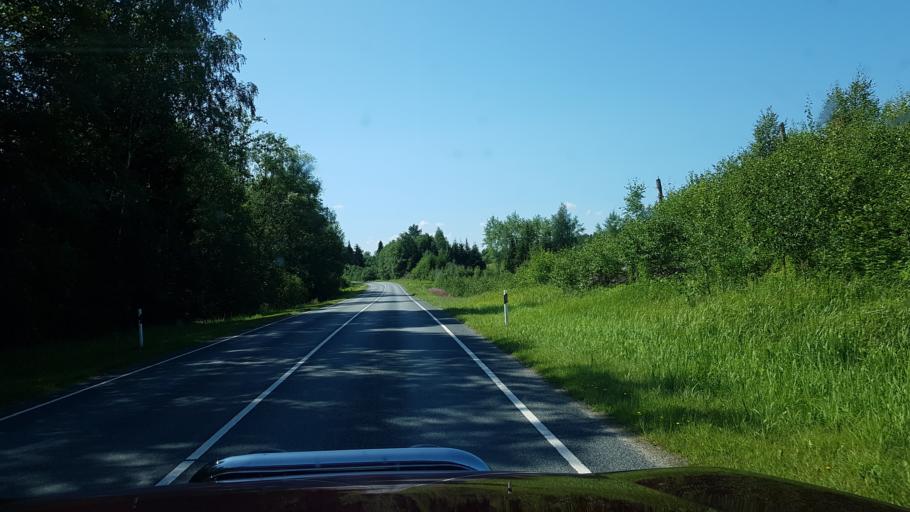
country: EE
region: Vorumaa
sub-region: Antsla vald
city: Vana-Antsla
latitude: 57.9635
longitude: 26.4558
